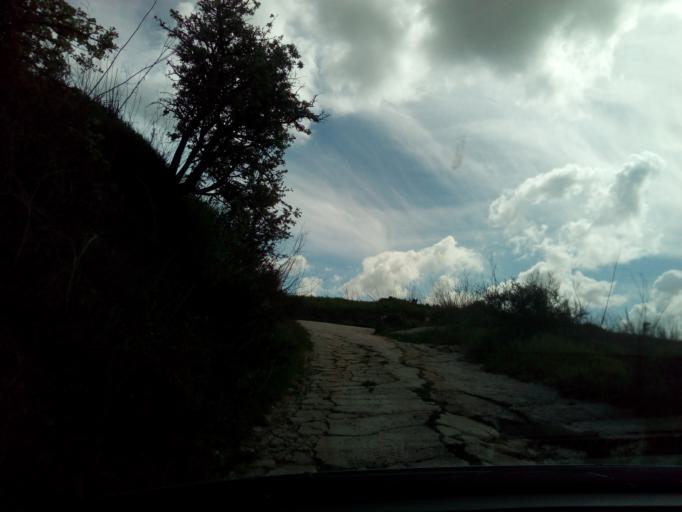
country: CY
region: Pafos
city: Tala
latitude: 34.8971
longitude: 32.4925
